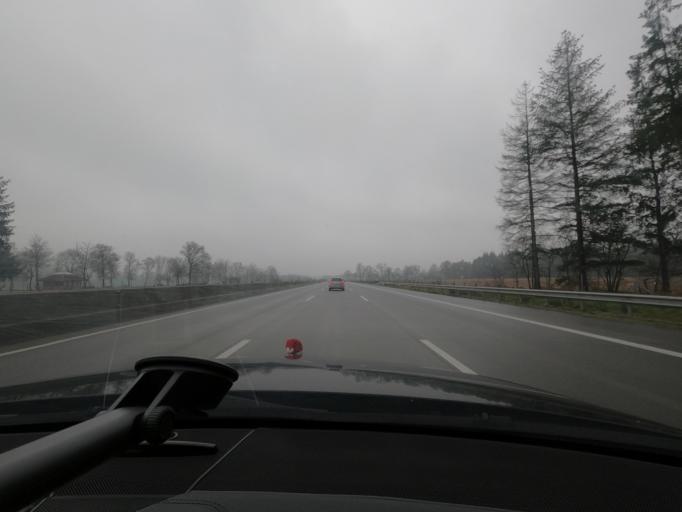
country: DE
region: Schleswig-Holstein
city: Bimohlen
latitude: 53.9244
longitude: 9.9401
